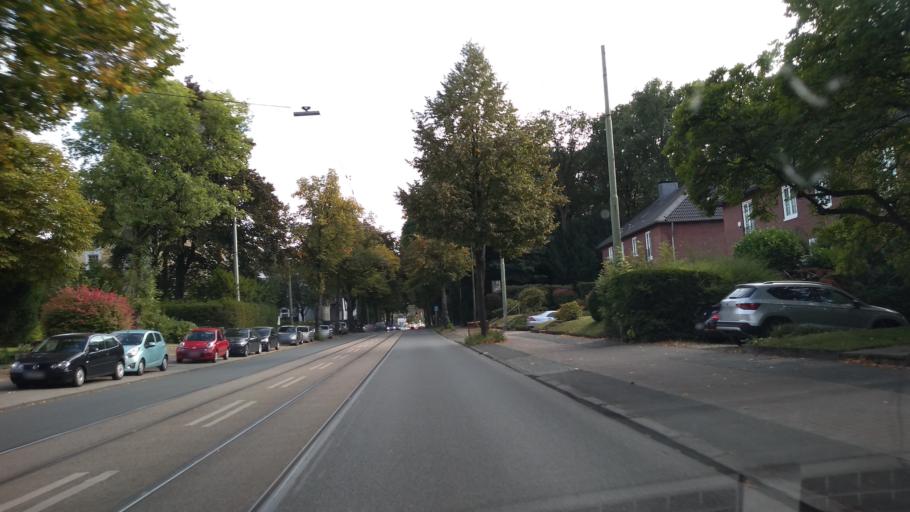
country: DE
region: North Rhine-Westphalia
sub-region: Regierungsbezirk Arnsberg
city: Bochum
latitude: 51.4495
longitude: 7.1936
